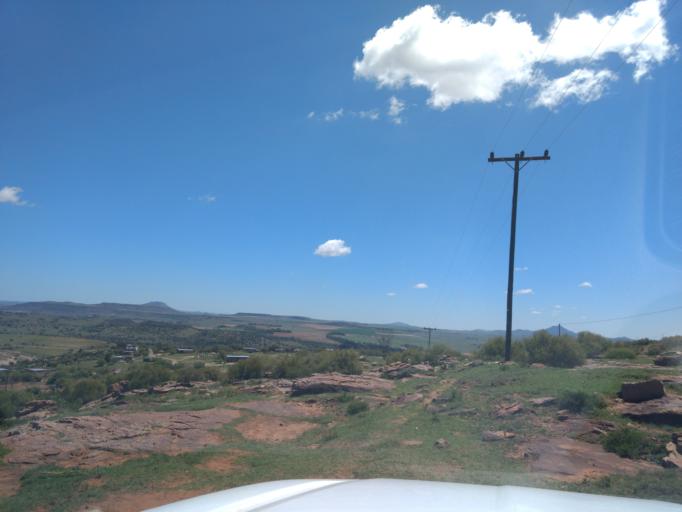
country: LS
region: Maseru
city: Maseru
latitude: -29.4568
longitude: 27.3772
